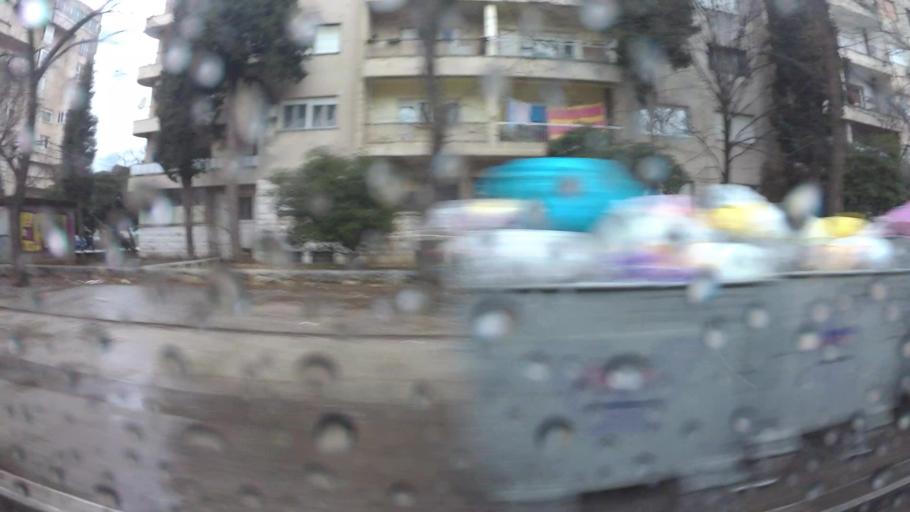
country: BA
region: Federation of Bosnia and Herzegovina
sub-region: Hercegovacko-Bosanski Kanton
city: Mostar
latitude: 43.3482
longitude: 17.8088
